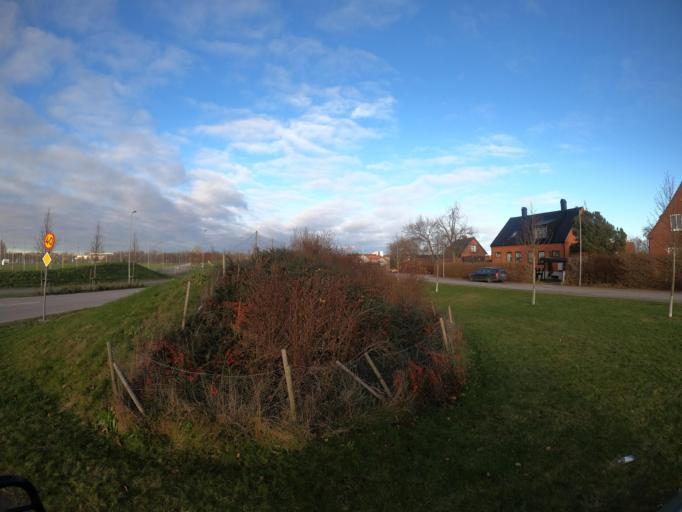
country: SE
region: Skane
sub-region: Svedala Kommun
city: Svedala
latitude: 55.5017
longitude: 13.2389
